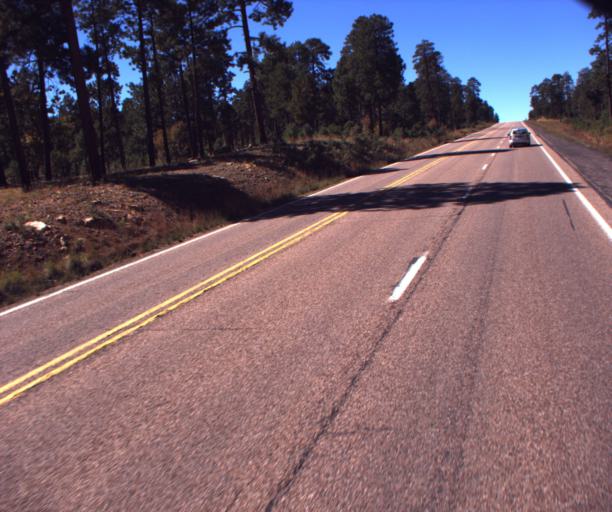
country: US
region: Arizona
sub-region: Navajo County
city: Heber-Overgaard
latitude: 34.3359
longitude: -110.7429
